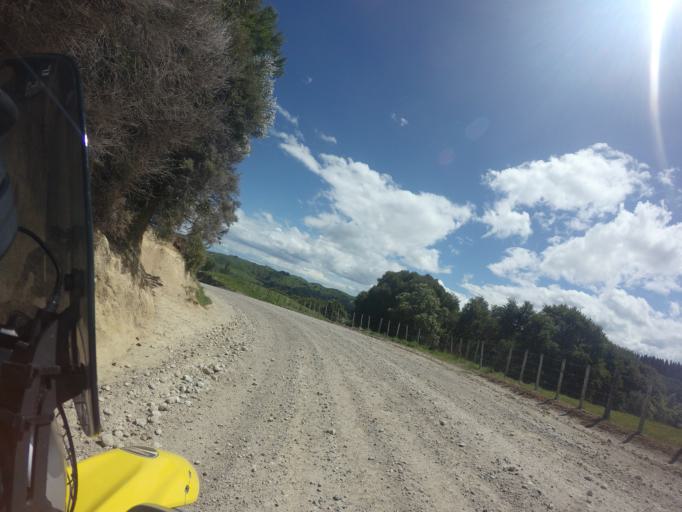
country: NZ
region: Hawke's Bay
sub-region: Wairoa District
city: Wairoa
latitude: -38.9698
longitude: 177.7029
